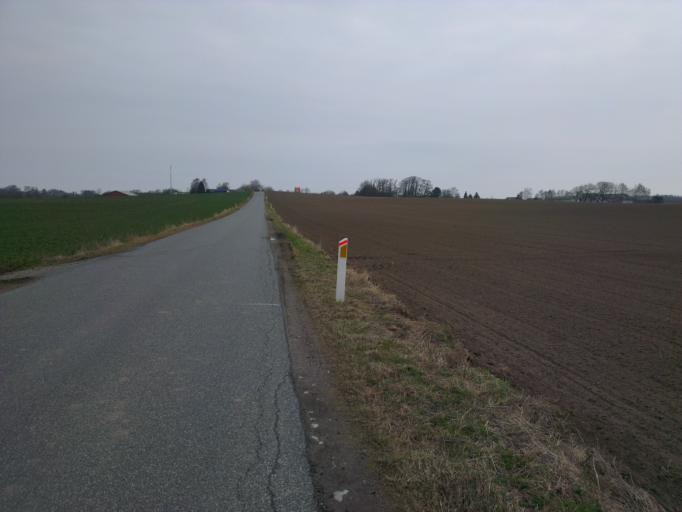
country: DK
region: Capital Region
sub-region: Frederikssund Kommune
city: Skibby
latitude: 55.7532
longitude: 11.9097
